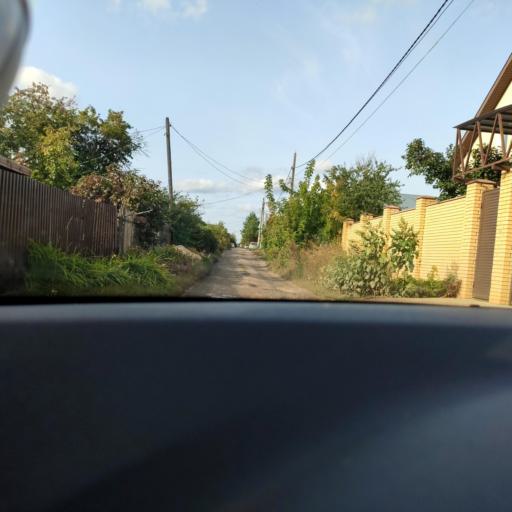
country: RU
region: Samara
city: Petra-Dubrava
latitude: 53.2821
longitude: 50.2955
